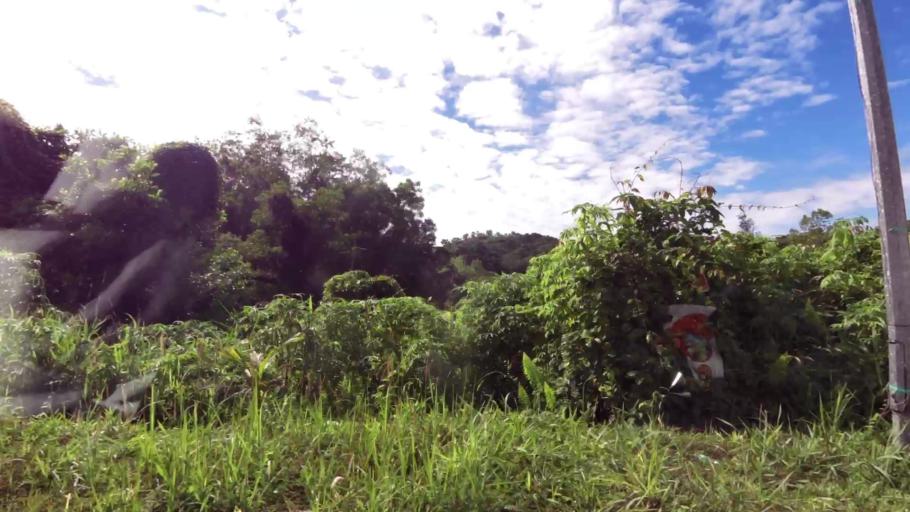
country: BN
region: Brunei and Muara
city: Bandar Seri Begawan
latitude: 4.9029
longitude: 114.9730
